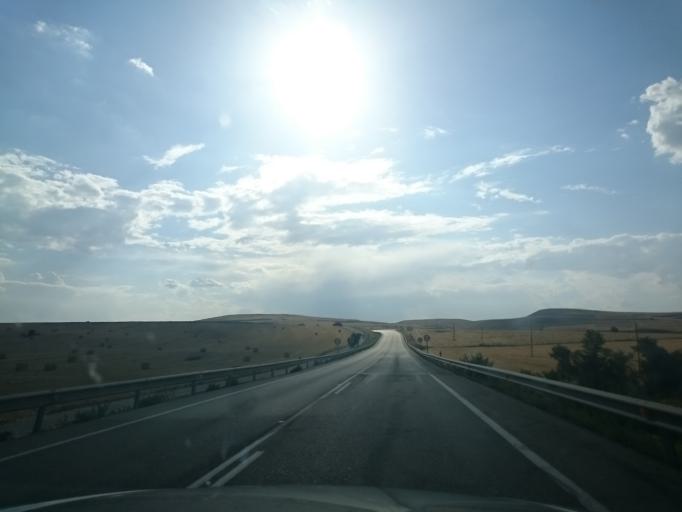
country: ES
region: Castille and Leon
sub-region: Provincia de Burgos
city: Fresnena
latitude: 42.4308
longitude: -3.1251
